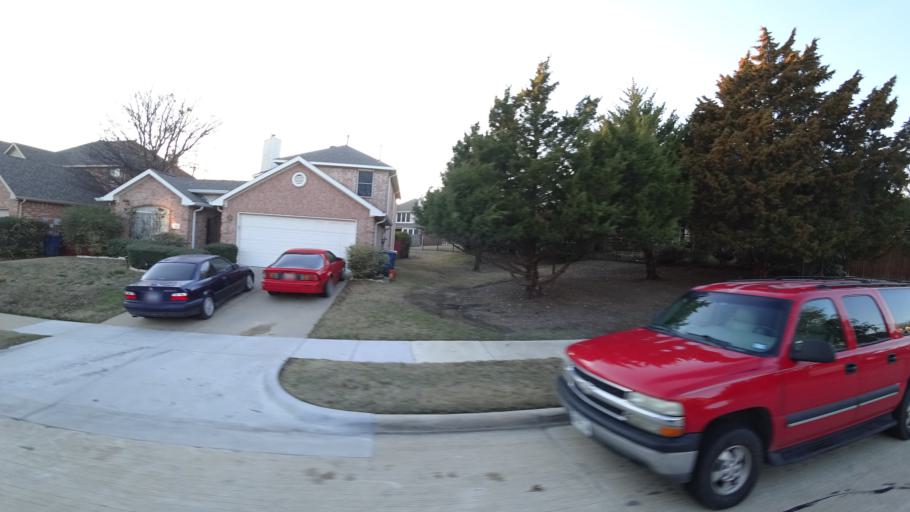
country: US
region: Texas
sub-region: Dallas County
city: Coppell
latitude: 32.9902
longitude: -96.9949
